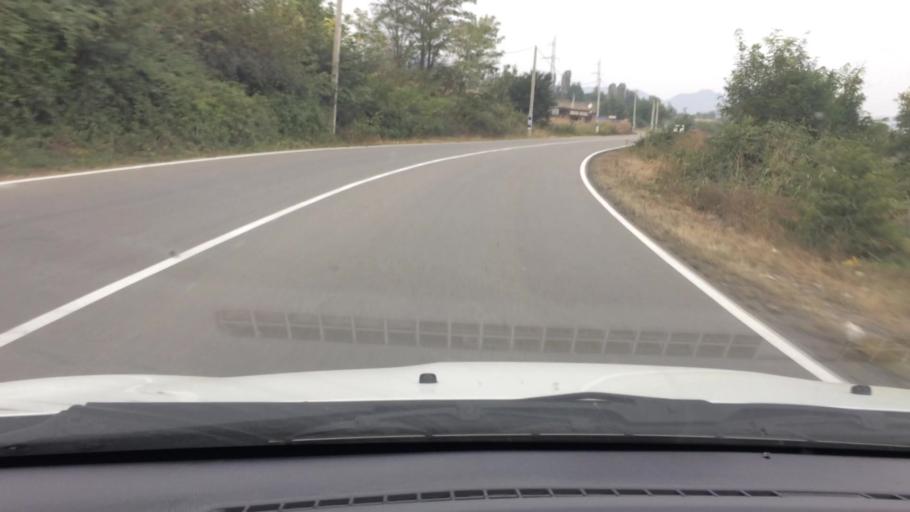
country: AM
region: Tavush
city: Bagratashen
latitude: 41.2659
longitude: 44.7921
